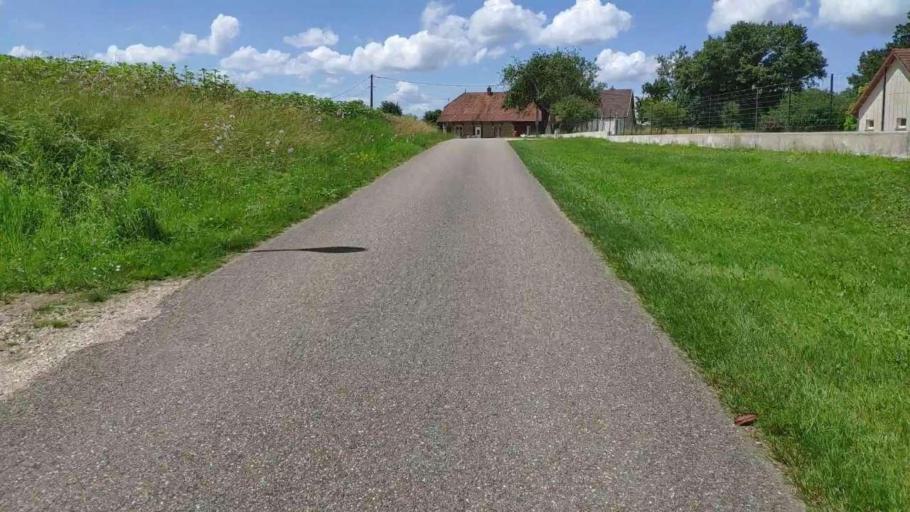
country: FR
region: Franche-Comte
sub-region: Departement du Jura
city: Bletterans
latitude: 46.8472
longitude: 5.4699
